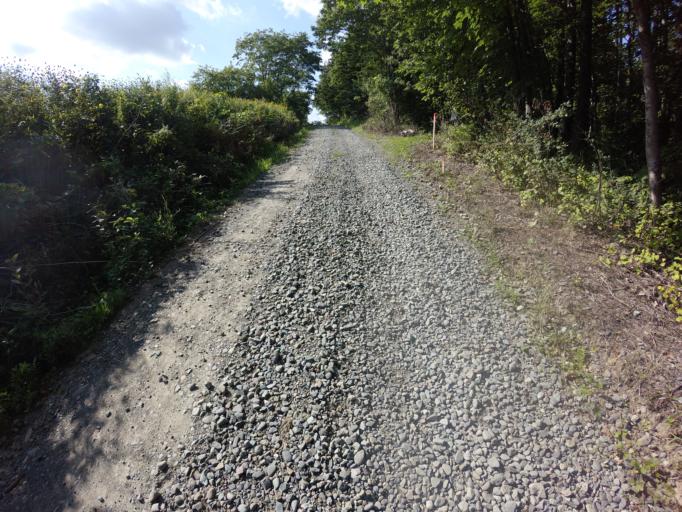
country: JP
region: Hokkaido
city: Iwamizawa
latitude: 43.1934
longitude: 141.8170
